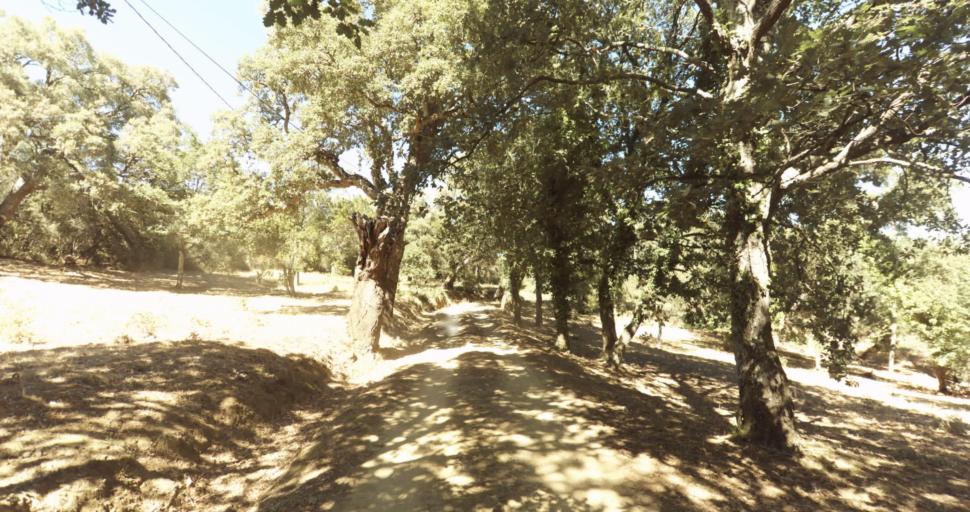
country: FR
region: Provence-Alpes-Cote d'Azur
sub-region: Departement du Var
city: La Croix-Valmer
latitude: 43.2243
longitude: 6.5534
